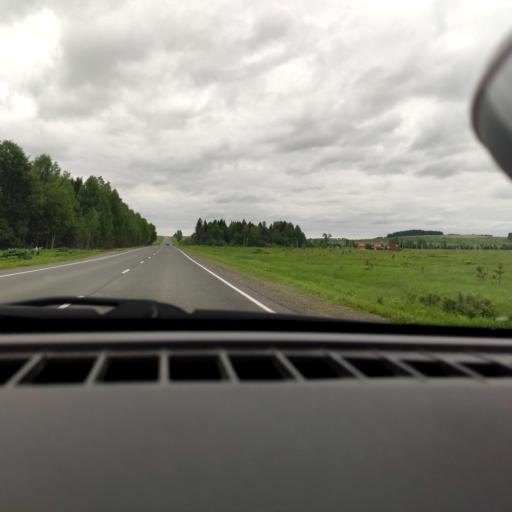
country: RU
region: Perm
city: Ust'-Kachka
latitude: 57.9635
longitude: 55.7280
